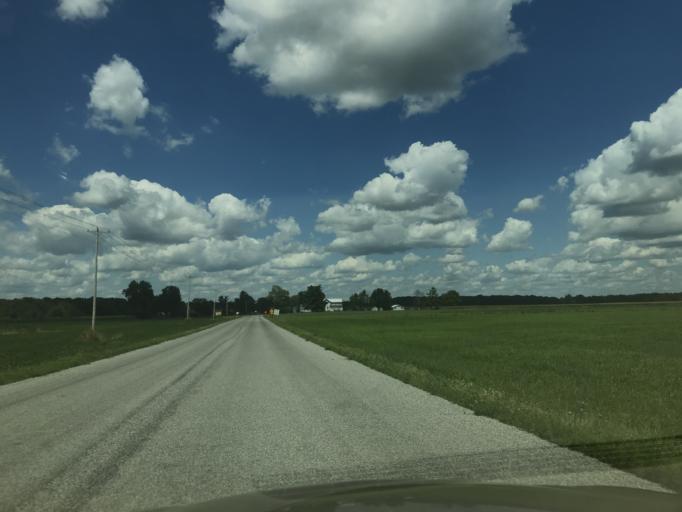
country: US
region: Michigan
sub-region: Ingham County
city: Holt
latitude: 42.5939
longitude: -84.5625
